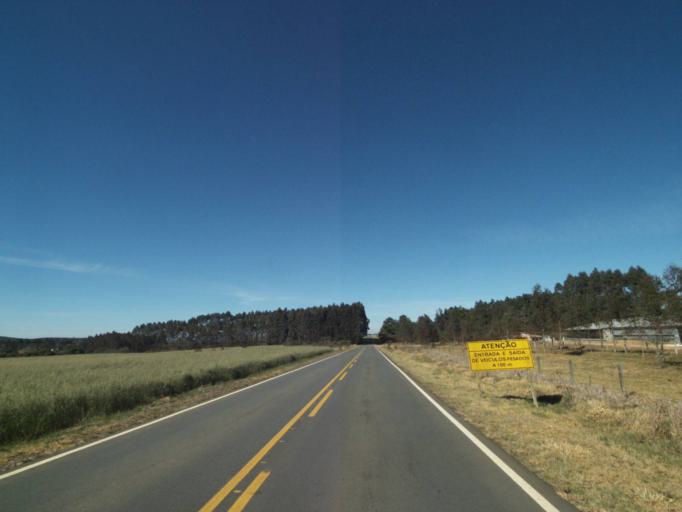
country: BR
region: Parana
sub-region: Castro
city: Castro
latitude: -24.7135
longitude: -50.1924
